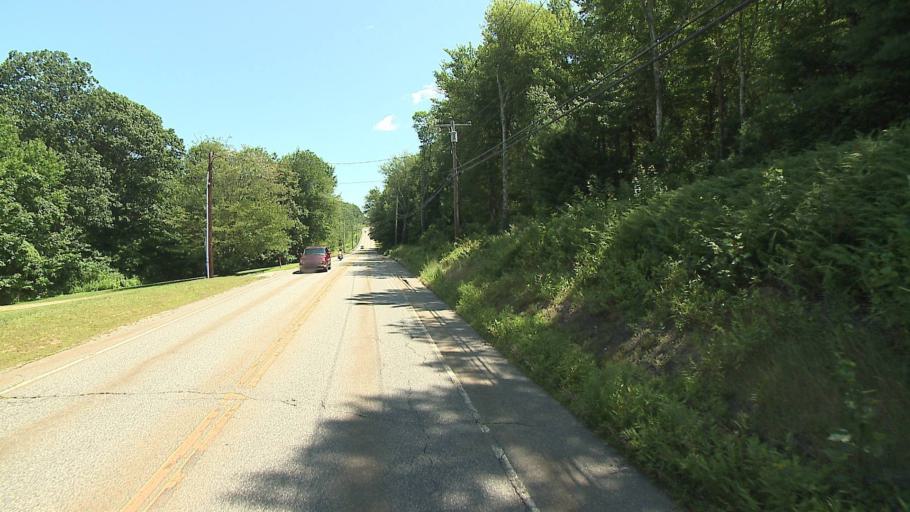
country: US
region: Connecticut
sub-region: Hartford County
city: Collinsville
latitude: 41.7757
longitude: -72.9806
